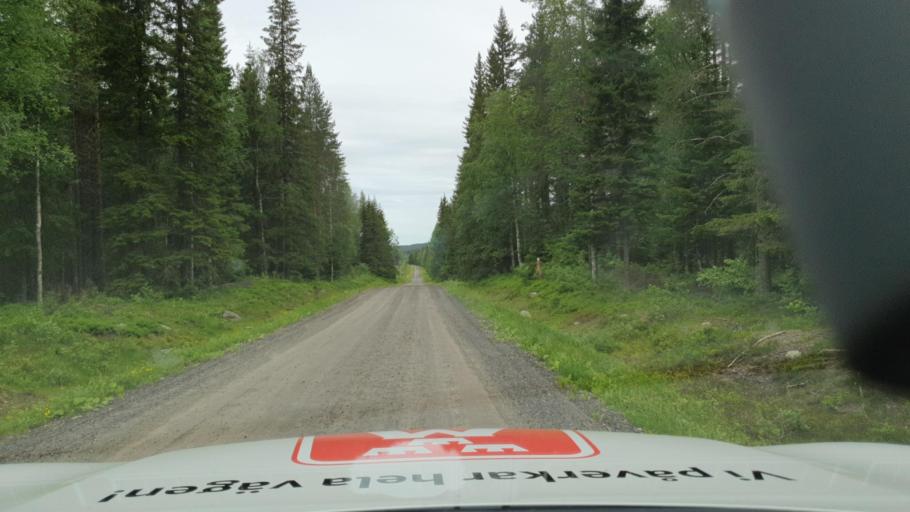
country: SE
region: Vaesterbotten
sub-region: Skelleftea Kommun
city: Burtraesk
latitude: 64.3772
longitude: 20.6152
